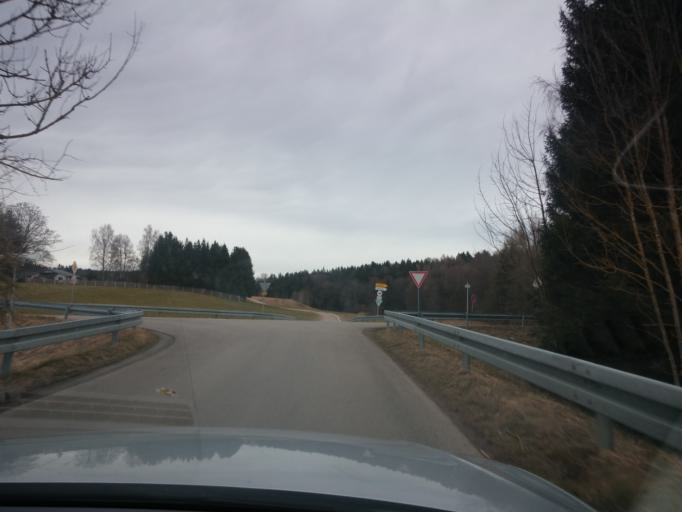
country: DE
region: Bavaria
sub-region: Upper Bavaria
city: Moosach
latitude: 48.0235
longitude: 11.8539
